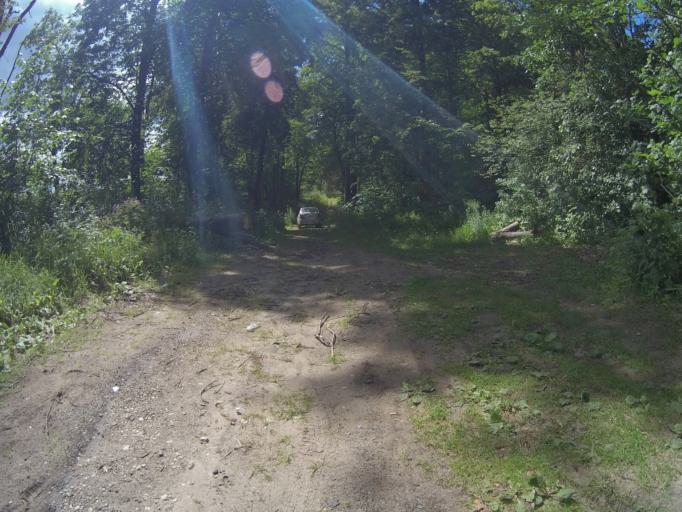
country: RU
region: Vladimir
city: Raduzhnyy
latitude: 56.0520
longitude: 40.3005
